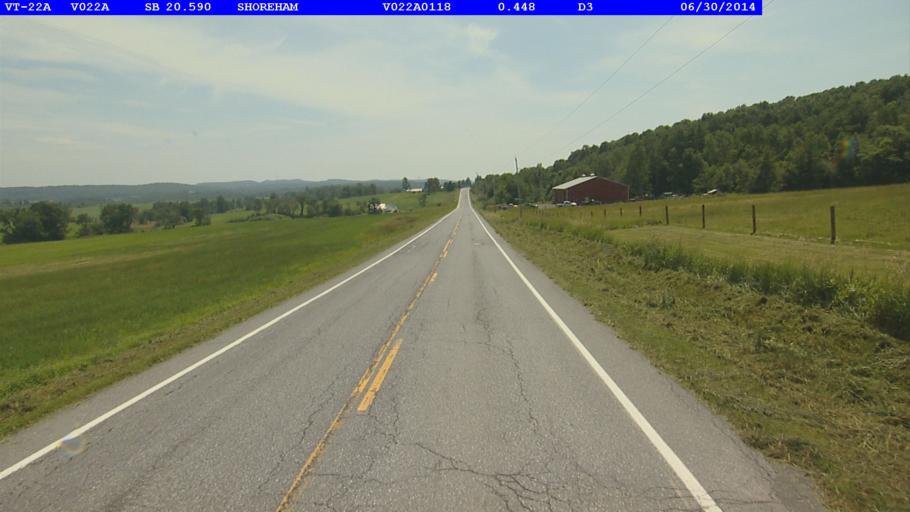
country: US
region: New York
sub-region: Essex County
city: Ticonderoga
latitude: 43.8558
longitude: -73.3093
